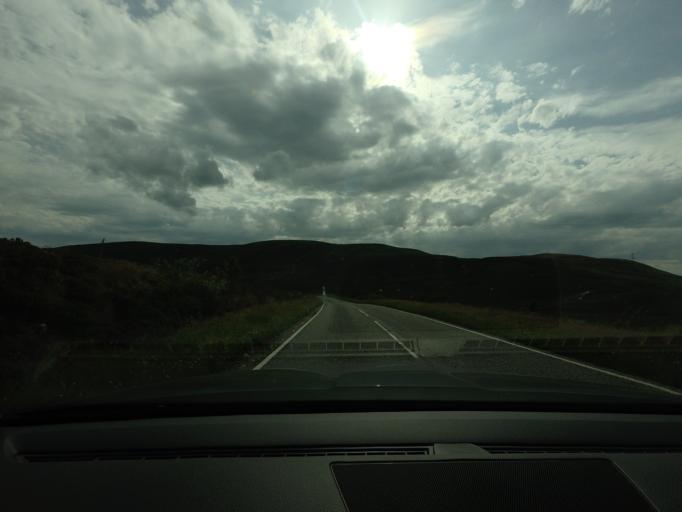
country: GB
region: Scotland
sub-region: Highland
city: Alness
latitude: 57.8367
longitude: -4.2717
